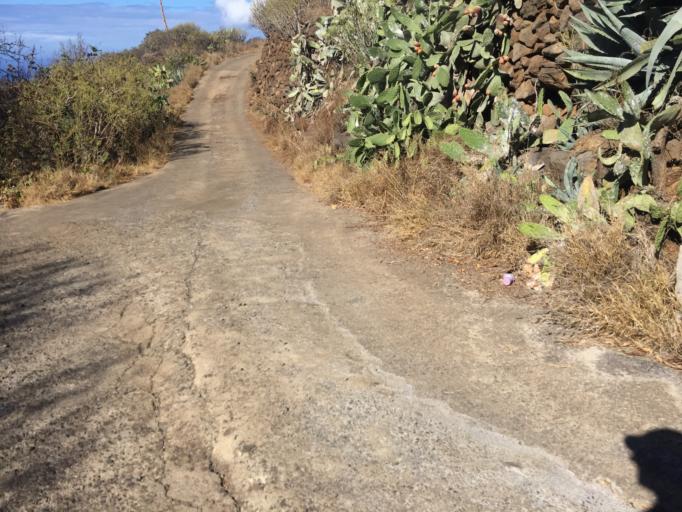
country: ES
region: Canary Islands
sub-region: Provincia de Santa Cruz de Tenerife
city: Tijarafe
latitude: 28.7229
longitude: -17.9675
